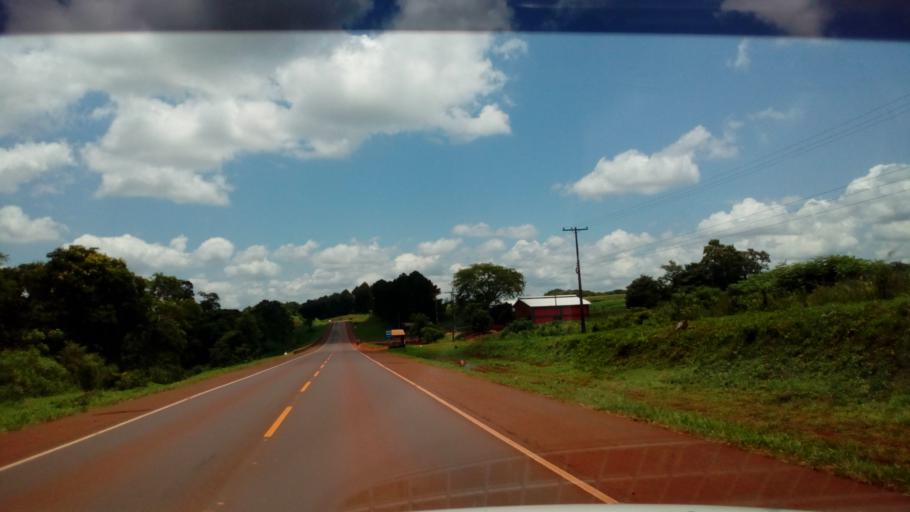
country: PY
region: Itapua
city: Arquitecto Tomas Romero Pereira
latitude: -26.4499
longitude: -55.2563
